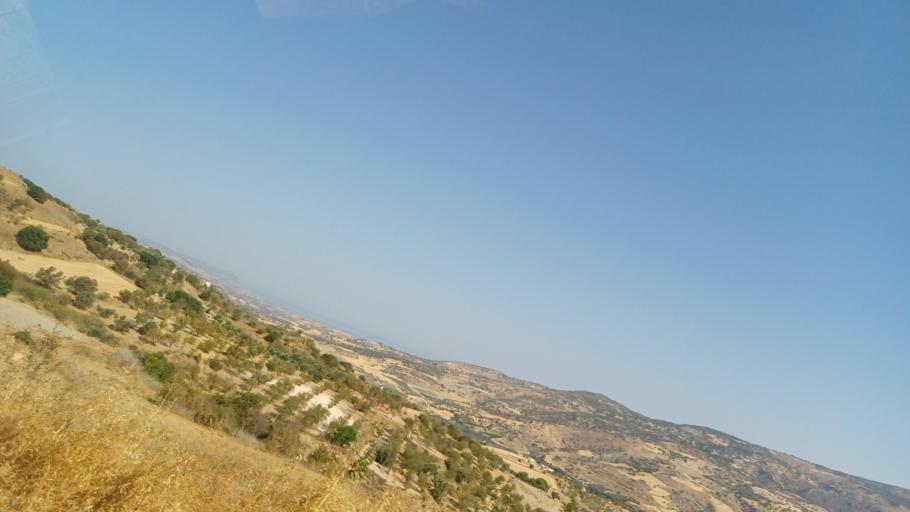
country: CY
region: Pafos
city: Polis
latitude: 34.9405
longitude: 32.5127
